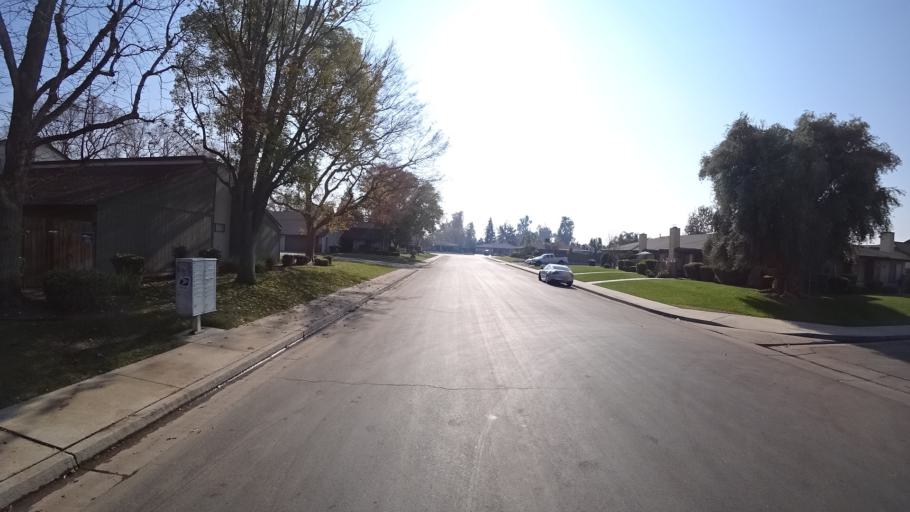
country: US
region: California
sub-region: Kern County
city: Greenacres
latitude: 35.3289
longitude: -119.0763
